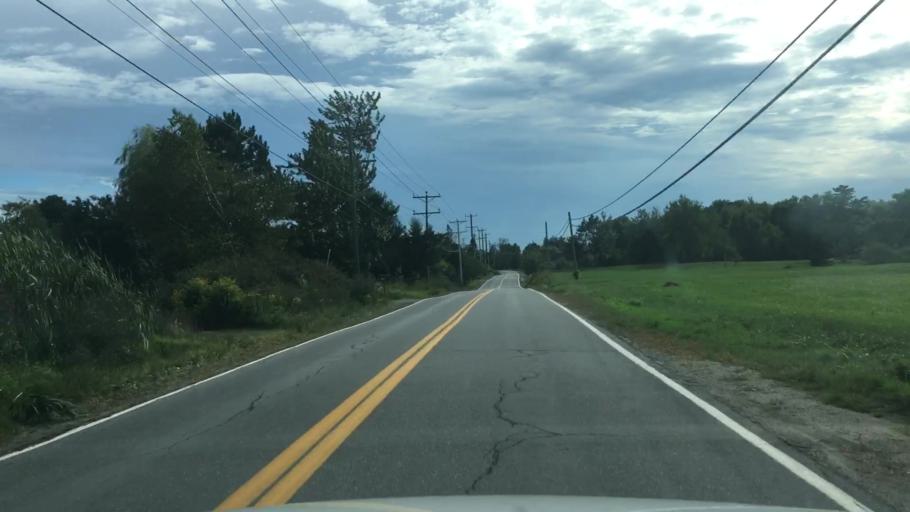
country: US
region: Maine
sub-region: Hancock County
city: Ellsworth
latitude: 44.5041
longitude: -68.4185
